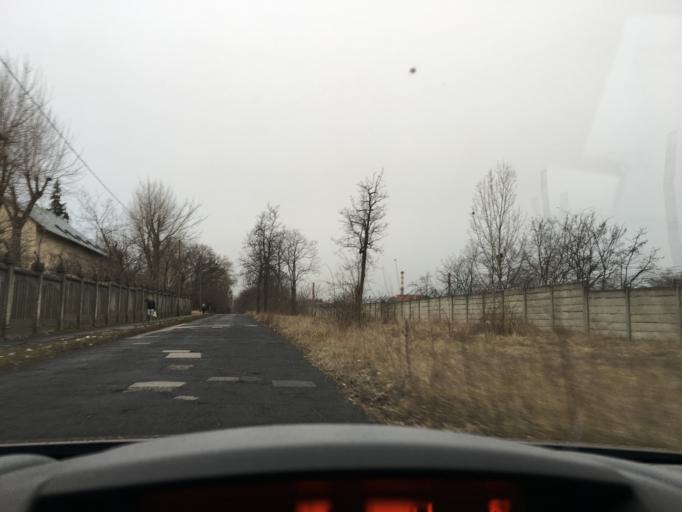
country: HU
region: Budapest
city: Budapest X. keruelet
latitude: 47.4882
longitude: 19.1627
